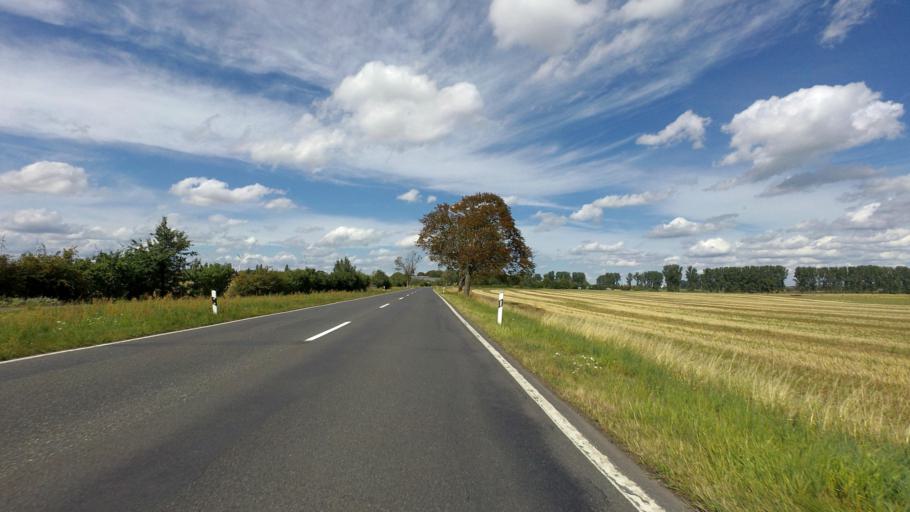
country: DE
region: Brandenburg
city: Wustermark
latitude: 52.5266
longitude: 12.9332
